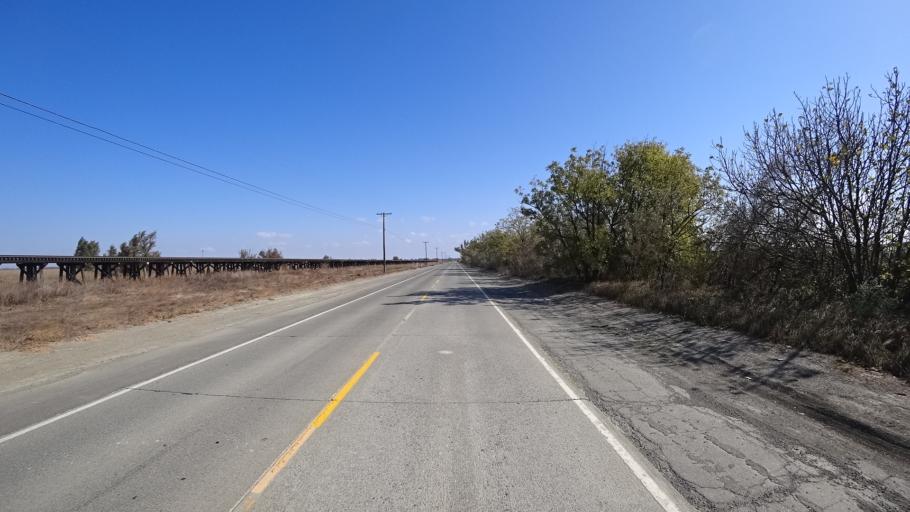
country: US
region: California
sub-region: Yolo County
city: Woodland
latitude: 38.6767
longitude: -121.6686
